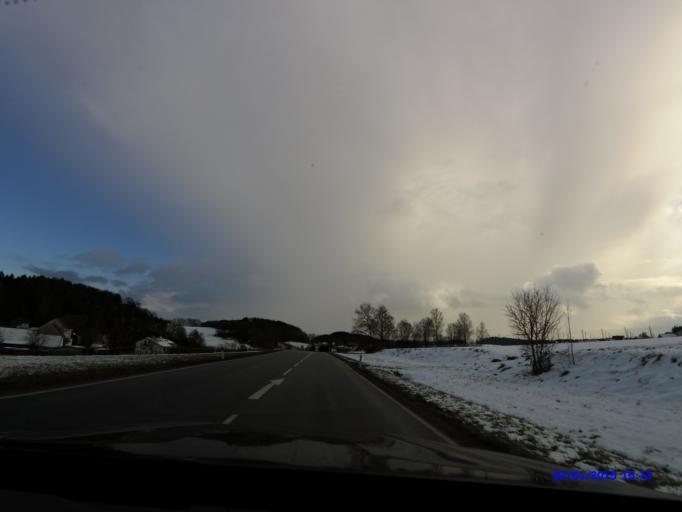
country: DE
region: Bavaria
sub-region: Lower Bavaria
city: Mainburg
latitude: 48.6220
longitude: 11.8098
